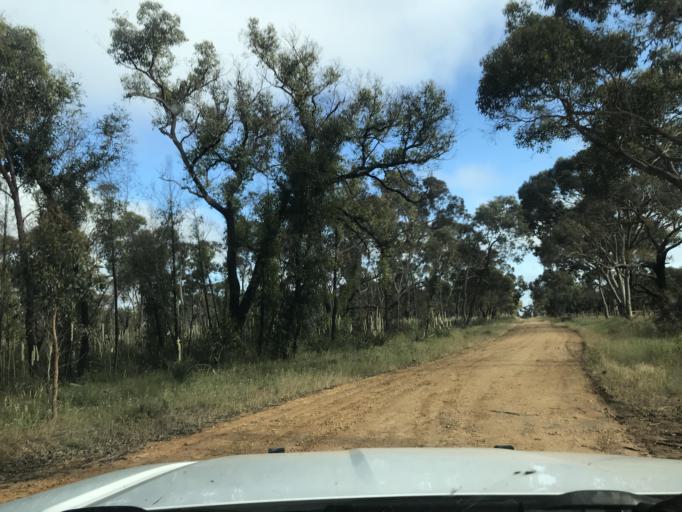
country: AU
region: South Australia
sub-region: Wattle Range
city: Penola
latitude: -37.1808
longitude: 141.1742
